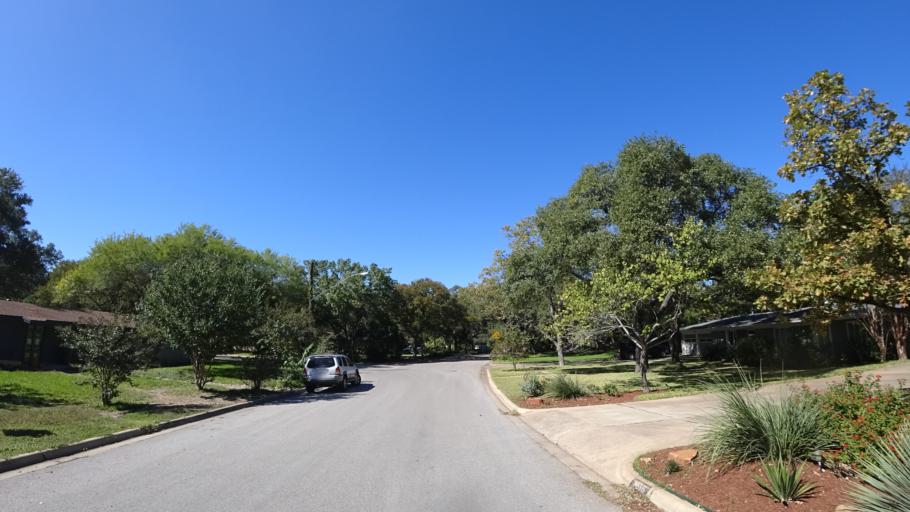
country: US
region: Texas
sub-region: Travis County
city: Austin
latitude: 30.3197
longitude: -97.7474
